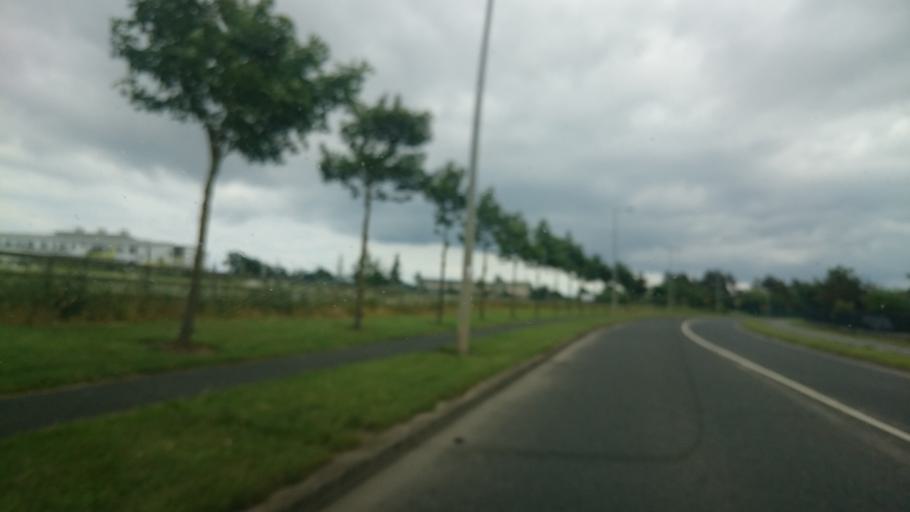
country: IE
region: Leinster
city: Lusk
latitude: 53.5299
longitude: -6.1609
